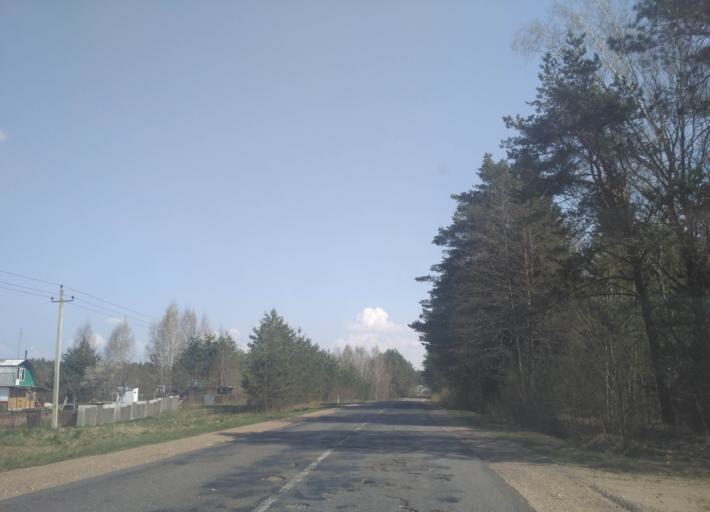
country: BY
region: Minsk
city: Loshnitsa
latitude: 54.4179
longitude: 28.6387
